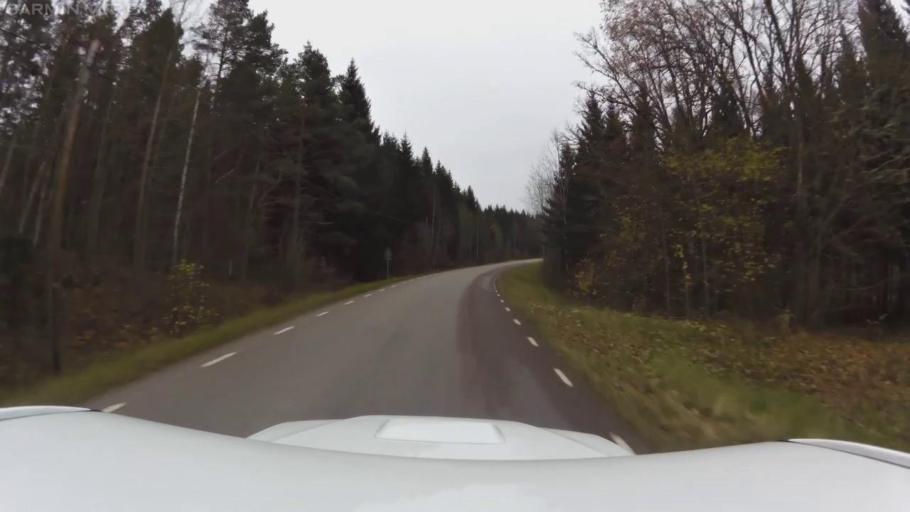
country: SE
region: OEstergoetland
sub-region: Linkopings Kommun
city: Vikingstad
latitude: 58.2516
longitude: 15.3850
